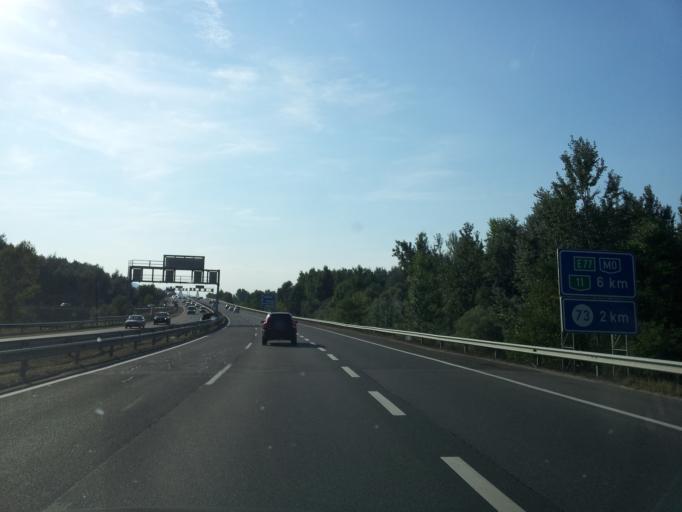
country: HU
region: Budapest
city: Budapest XV. keruelet
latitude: 47.5973
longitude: 19.1339
